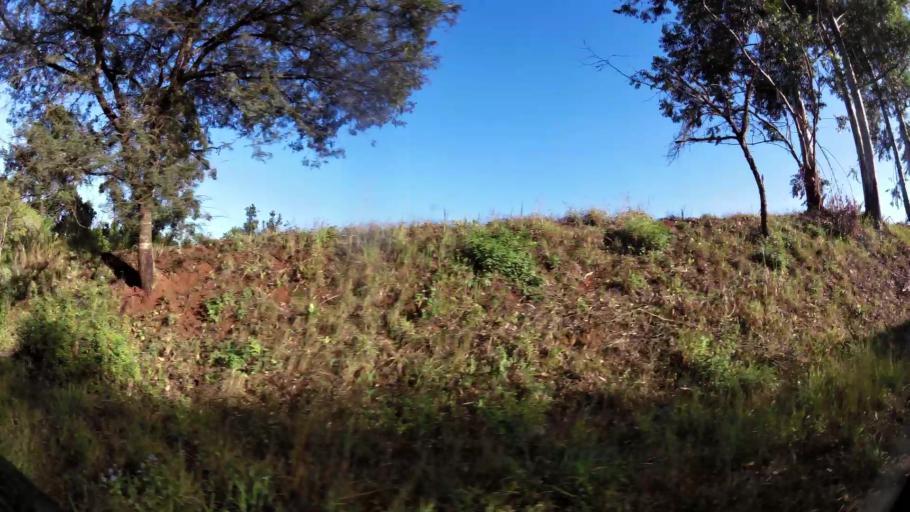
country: ZA
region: Limpopo
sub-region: Mopani District Municipality
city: Tzaneen
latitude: -23.8880
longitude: 30.0860
